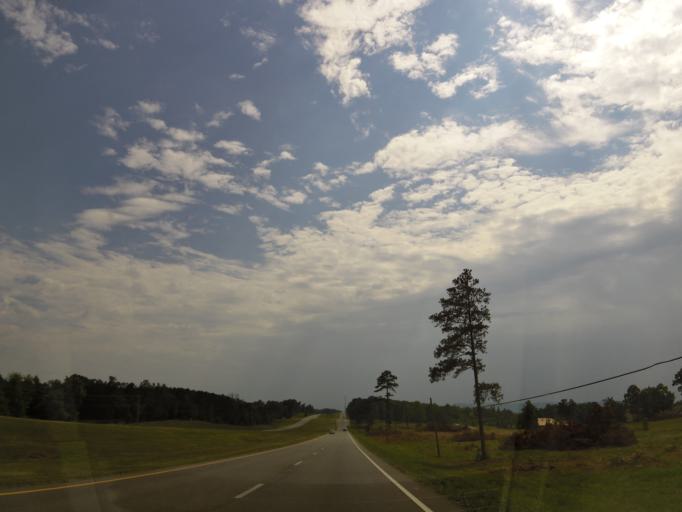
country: US
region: Alabama
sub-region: Jackson County
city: Stevenson
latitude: 34.8054
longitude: -85.8651
